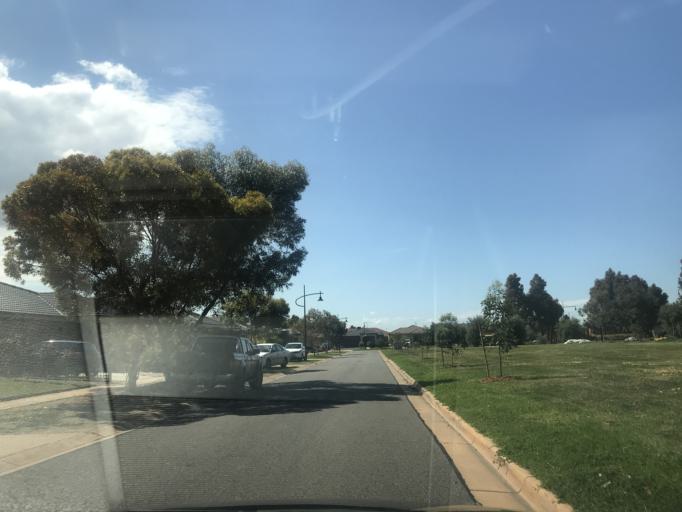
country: AU
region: Victoria
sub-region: Wyndham
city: Hoppers Crossing
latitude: -37.8920
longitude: 144.7199
